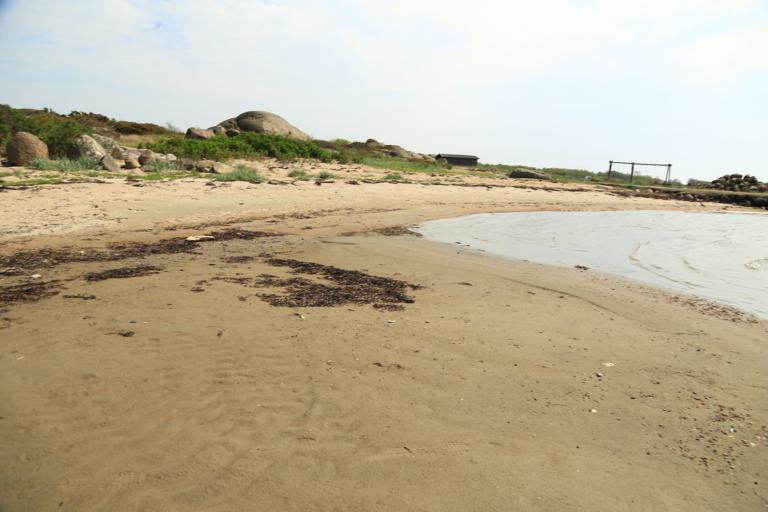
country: SE
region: Halland
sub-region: Varbergs Kommun
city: Varberg
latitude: 57.1415
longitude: 12.2152
